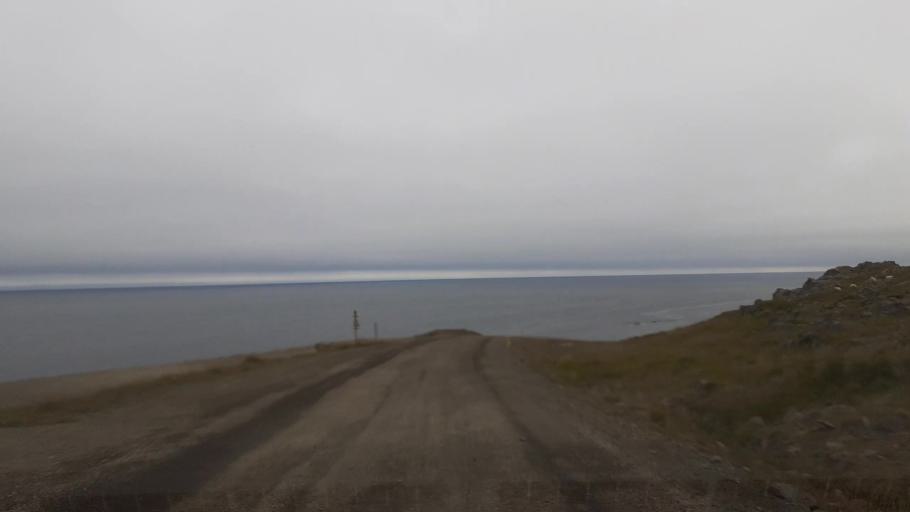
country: IS
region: Northwest
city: Saudarkrokur
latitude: 65.5252
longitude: -20.9635
